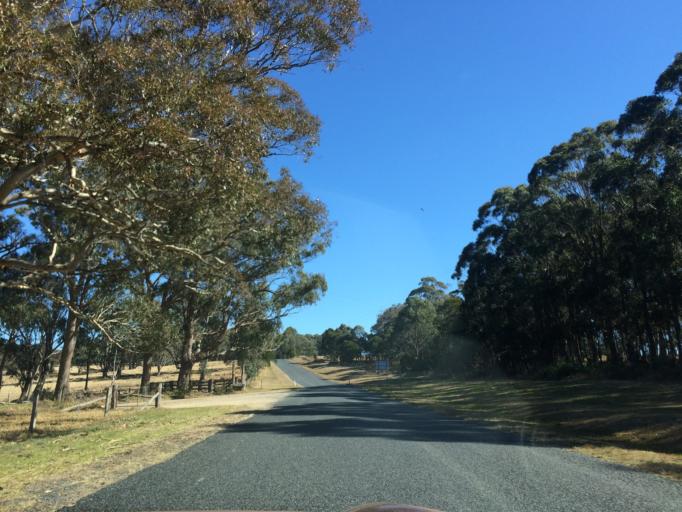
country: AU
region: Queensland
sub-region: Southern Downs
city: Stanthorpe
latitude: -28.6534
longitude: 152.0813
